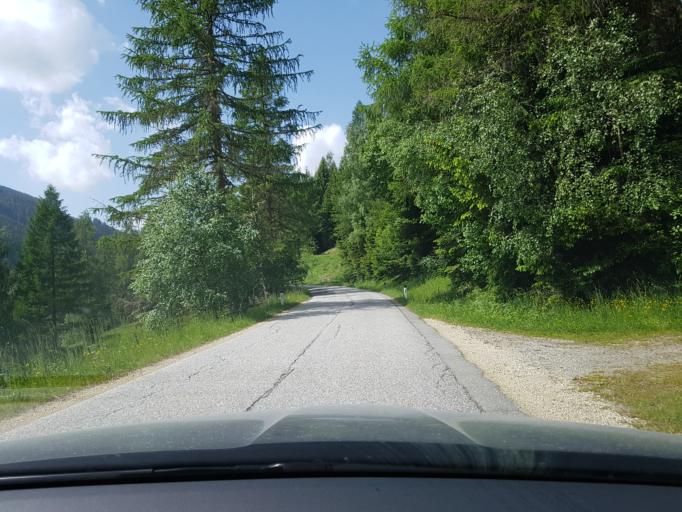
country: AT
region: Salzburg
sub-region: Politischer Bezirk Tamsweg
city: Thomatal
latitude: 47.0674
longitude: 13.7208
